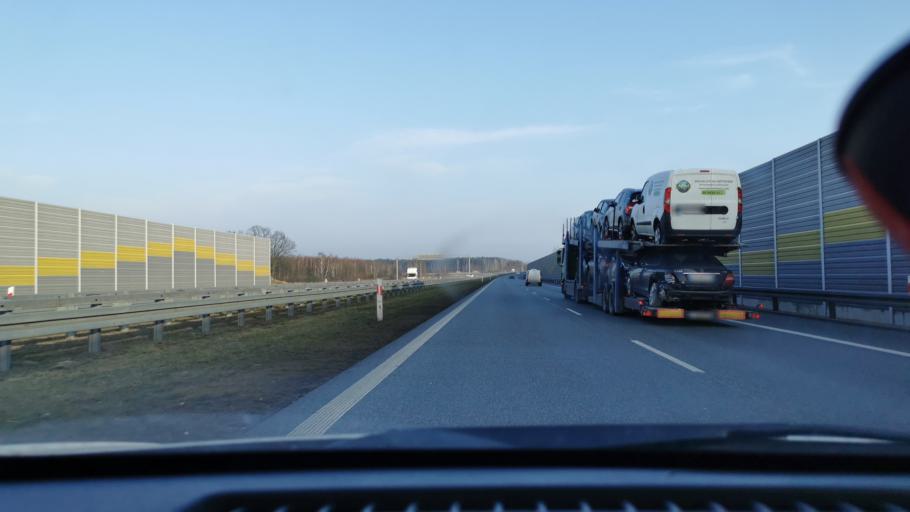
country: PL
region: Lodz Voivodeship
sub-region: Powiat zdunskowolski
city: Zapolice
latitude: 51.5970
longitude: 18.8482
